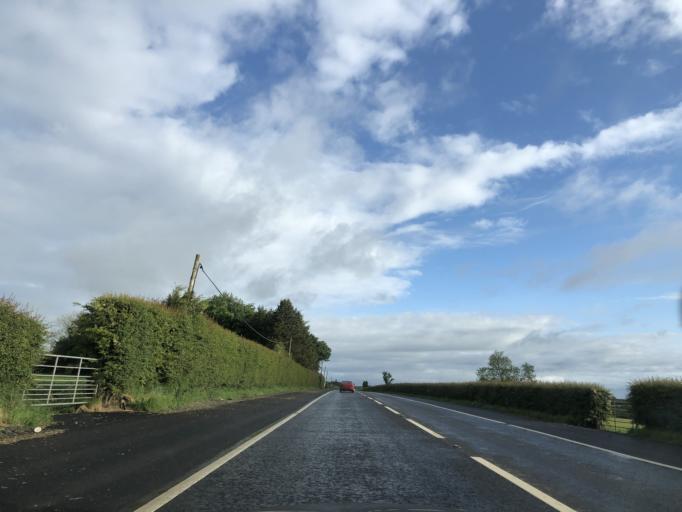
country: GB
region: Northern Ireland
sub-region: Ballymoney District
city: Ballymoney
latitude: 55.1347
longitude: -6.5590
